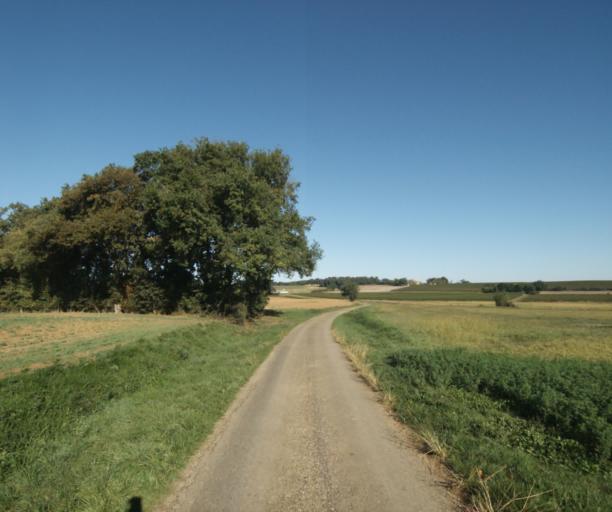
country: FR
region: Midi-Pyrenees
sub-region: Departement du Gers
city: Gondrin
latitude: 43.8253
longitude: 0.2654
